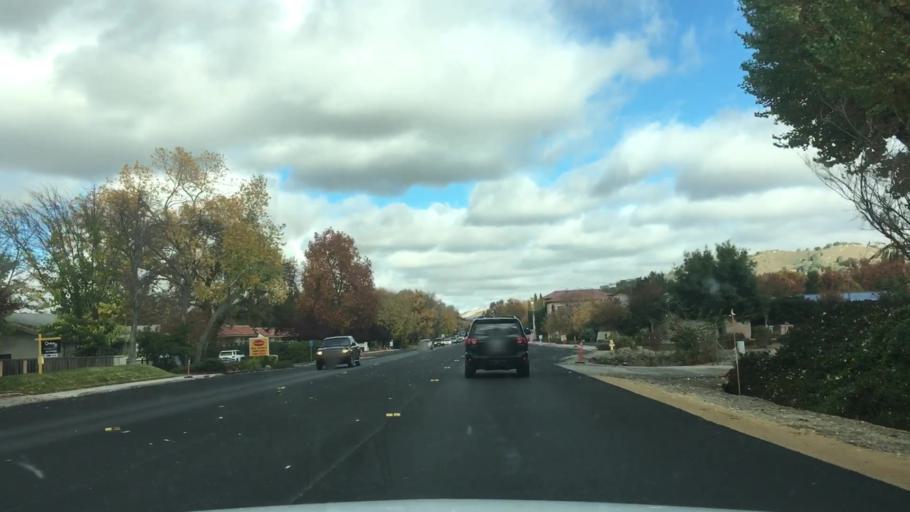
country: US
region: California
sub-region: San Luis Obispo County
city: Atascadero
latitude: 35.4770
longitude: -120.6675
